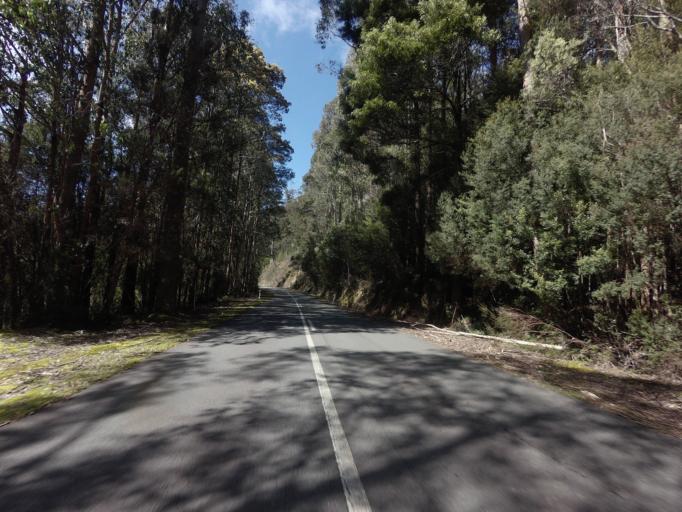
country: AU
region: Tasmania
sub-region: Derwent Valley
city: New Norfolk
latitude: -42.7375
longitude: 146.4896
